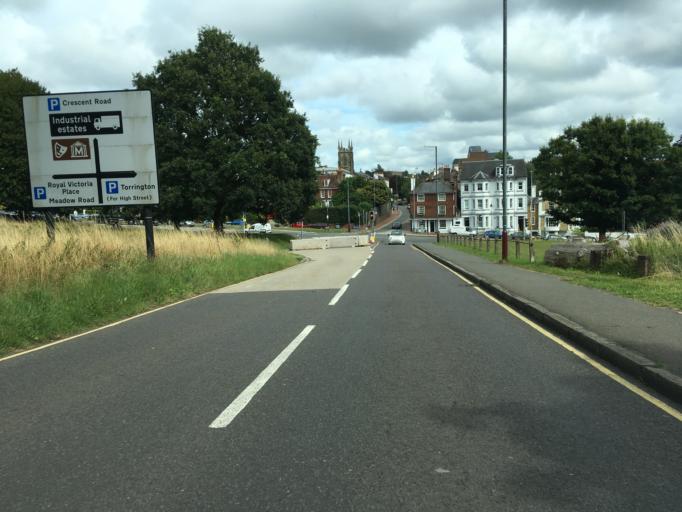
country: GB
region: England
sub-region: Kent
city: Royal Tunbridge Wells
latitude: 51.1324
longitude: 0.2576
